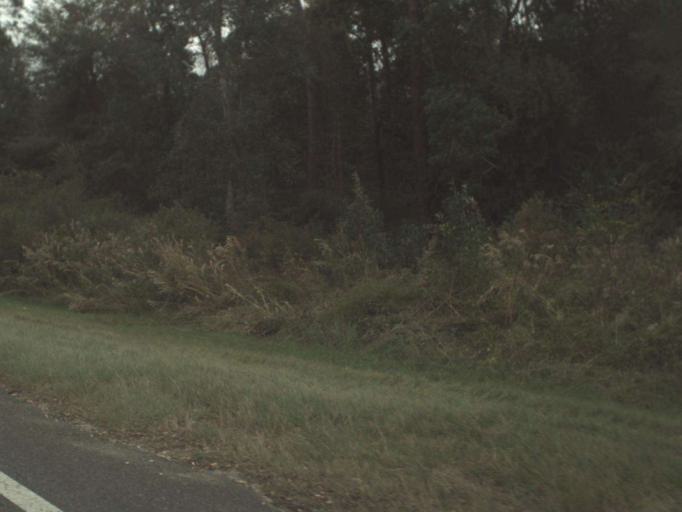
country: US
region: Florida
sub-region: Escambia County
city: Cantonment
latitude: 30.6181
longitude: -87.3246
